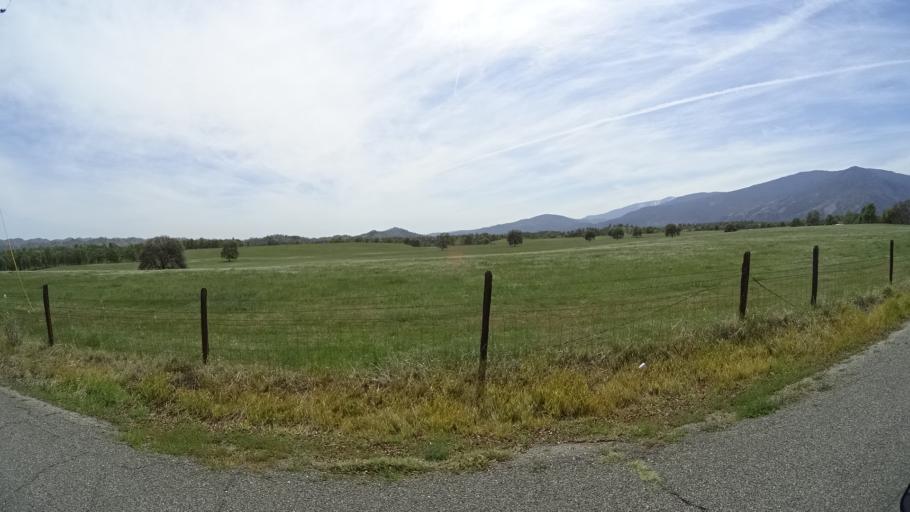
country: US
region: California
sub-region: Glenn County
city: Willows
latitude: 39.5919
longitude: -122.5712
